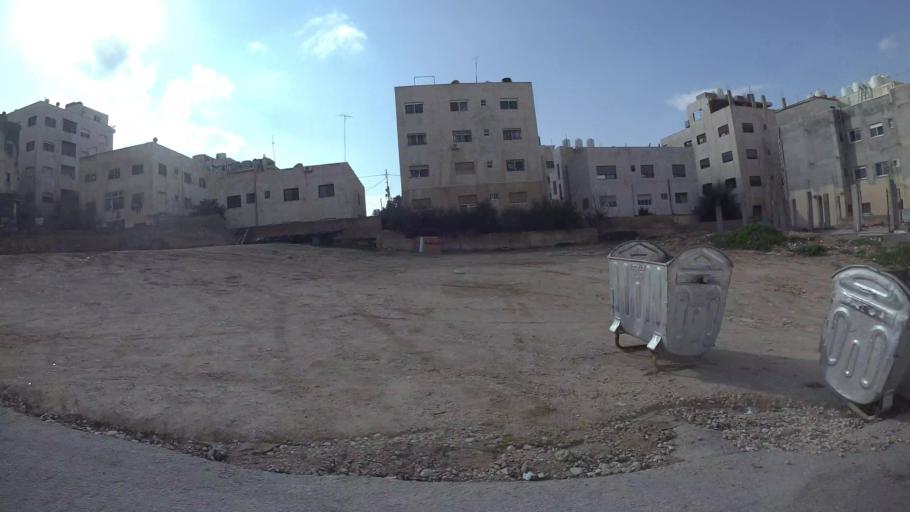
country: JO
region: Amman
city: Al Jubayhah
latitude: 32.0224
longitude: 35.8566
